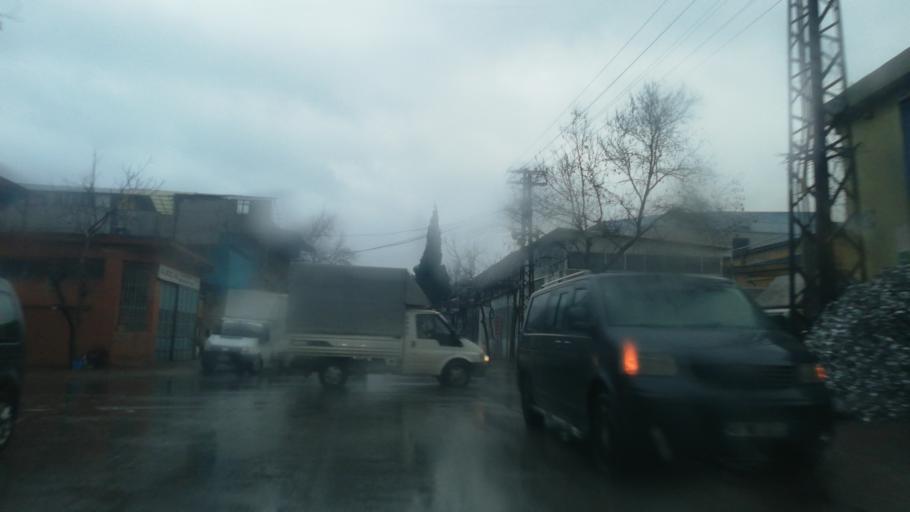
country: TR
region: Kahramanmaras
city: Kahramanmaras
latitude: 37.5611
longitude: 36.9598
